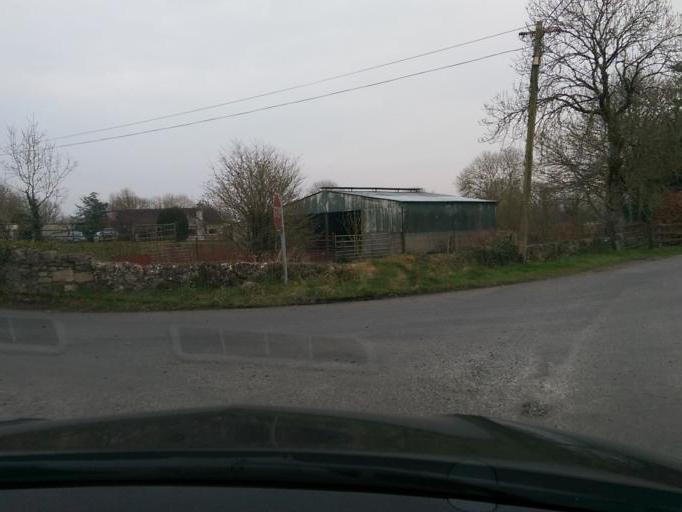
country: IE
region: Leinster
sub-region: An Longfort
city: Ballymahon
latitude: 53.5541
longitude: -7.7990
